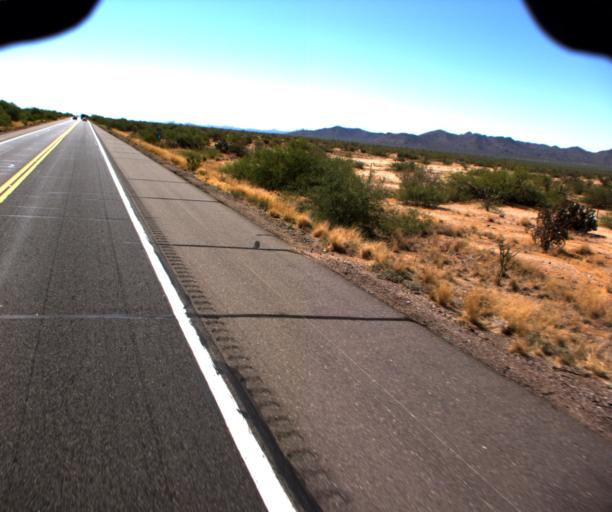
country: US
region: Arizona
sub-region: Yavapai County
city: Congress
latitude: 34.1416
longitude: -112.9767
